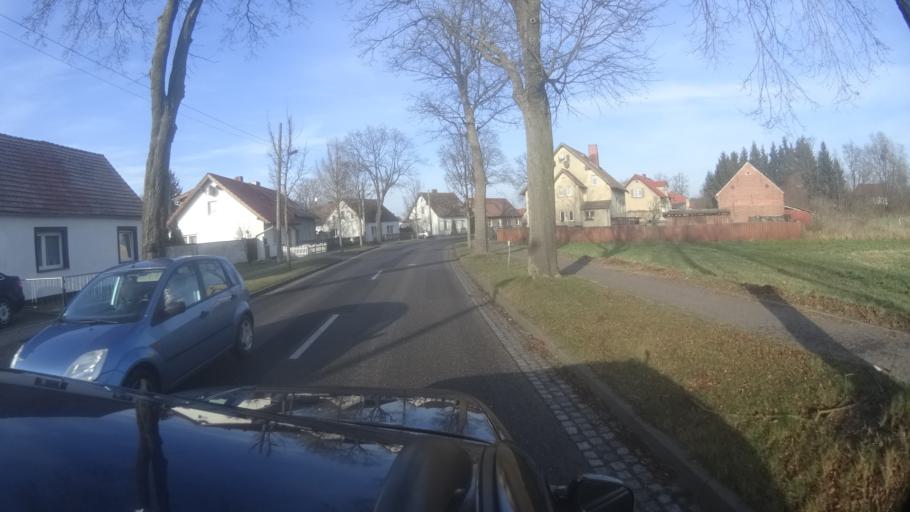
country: DE
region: Brandenburg
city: Kremmen
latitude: 52.7993
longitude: 13.0338
